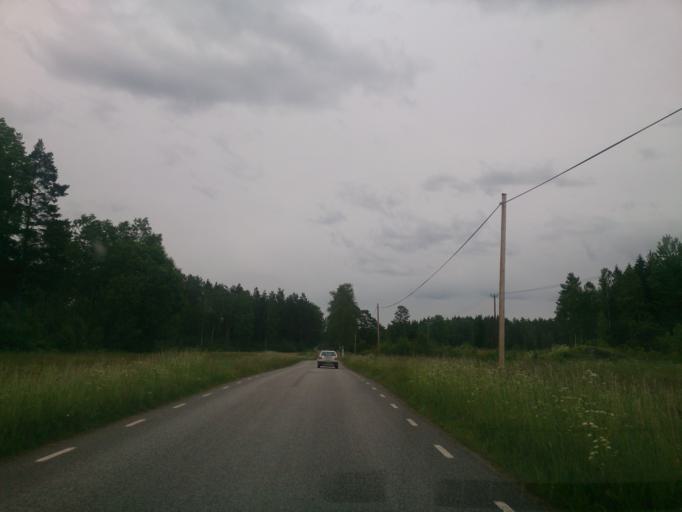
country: SE
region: OEstergoetland
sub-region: Valdemarsviks Kommun
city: Gusum
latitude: 58.3202
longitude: 16.3804
